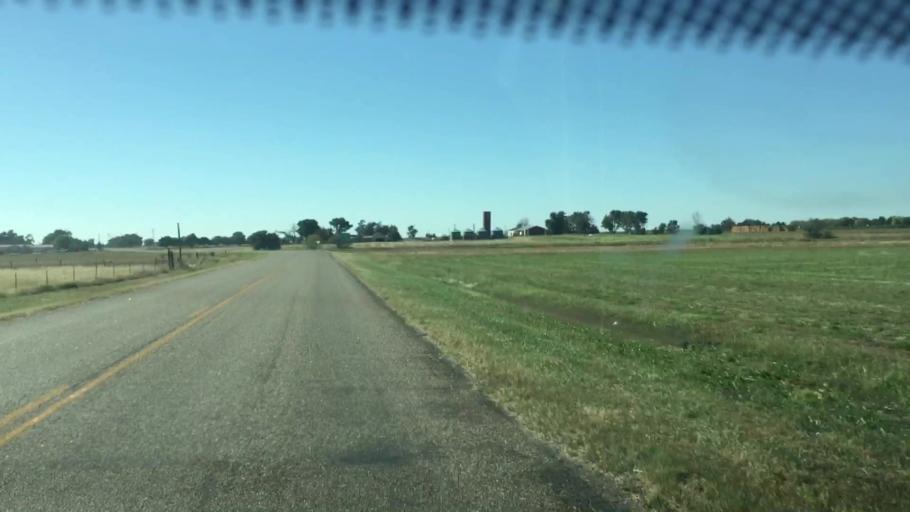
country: US
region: Colorado
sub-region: Prowers County
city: Lamar
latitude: 38.1174
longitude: -102.6077
